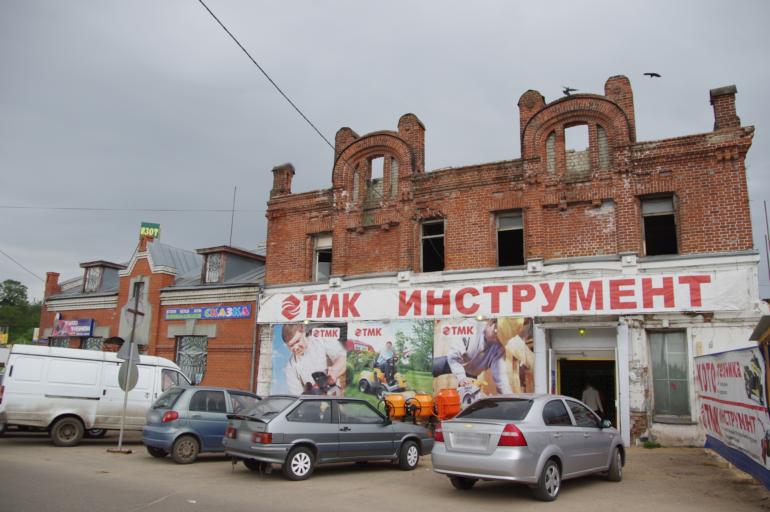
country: RU
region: Nizjnij Novgorod
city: Pavlovo
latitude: 55.9685
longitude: 43.0664
